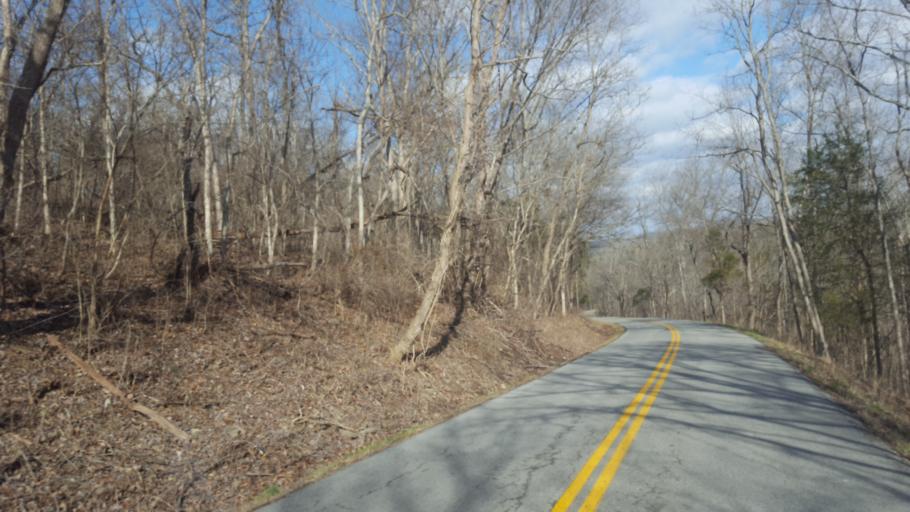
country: US
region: Kentucky
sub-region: Owen County
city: Owenton
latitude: 38.4288
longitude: -84.9638
